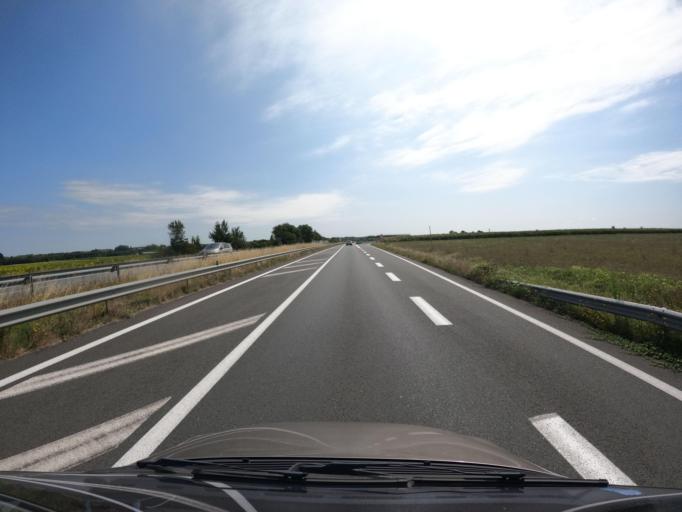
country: FR
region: Poitou-Charentes
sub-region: Departement des Deux-Sevres
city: Mauze-sur-le-Mignon
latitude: 46.1958
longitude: -0.6942
